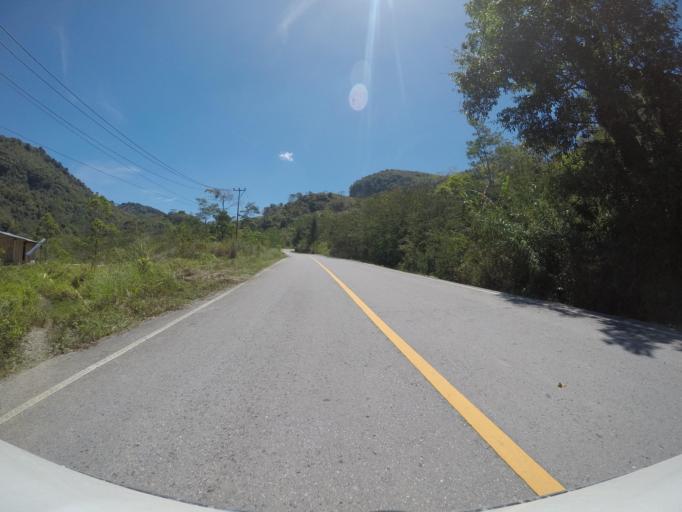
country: TL
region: Manatuto
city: Manatuto
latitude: -8.7691
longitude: 125.9660
